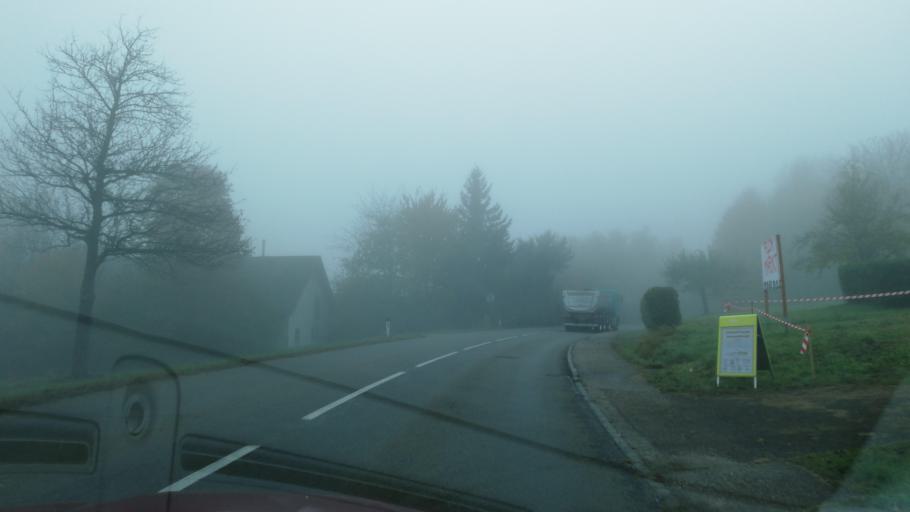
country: AT
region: Upper Austria
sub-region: Politischer Bezirk Grieskirchen
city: Bad Schallerbach
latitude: 48.1814
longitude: 13.9087
